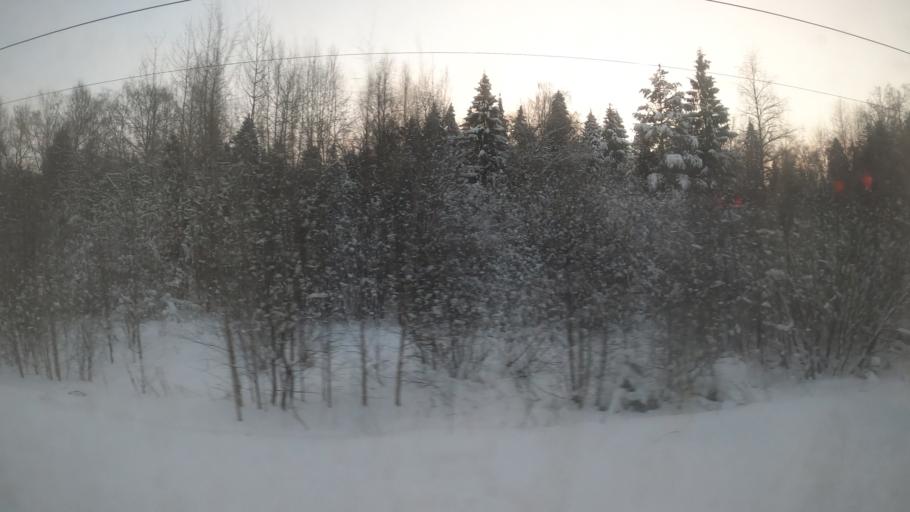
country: RU
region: Moskovskaya
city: Nekrasovskiy
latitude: 56.1185
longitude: 37.5130
